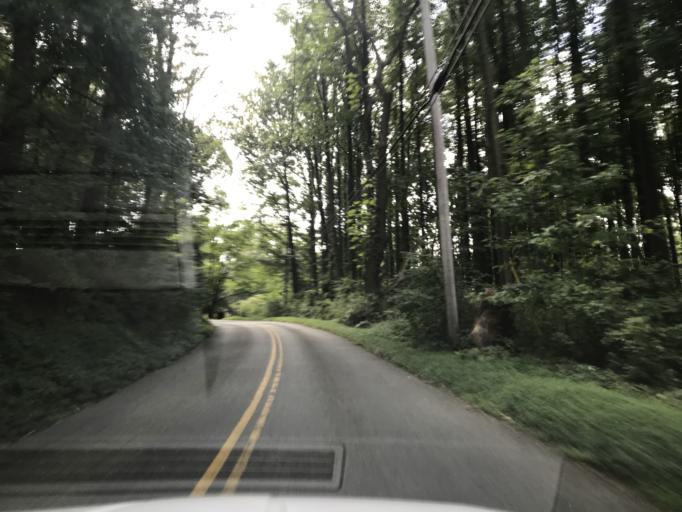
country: US
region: Maryland
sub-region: Harford County
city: Fallston
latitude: 39.5321
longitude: -76.4302
